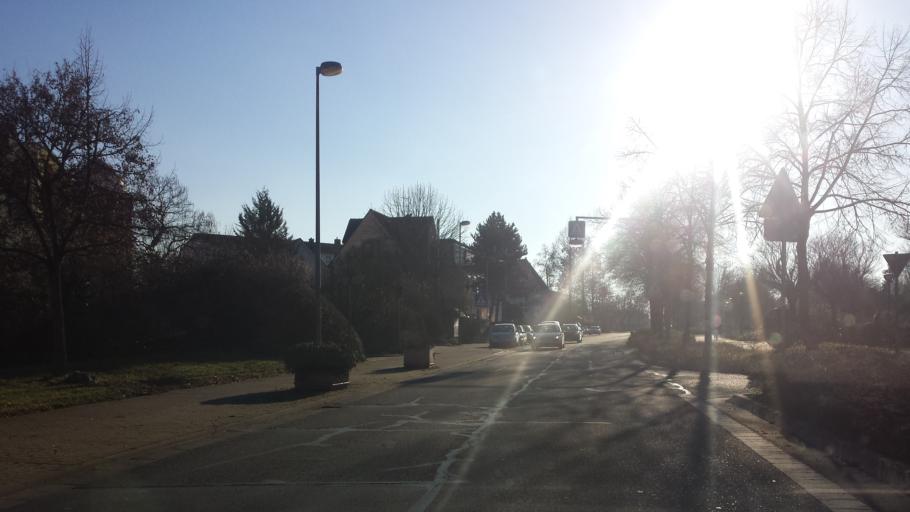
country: DE
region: Baden-Wuerttemberg
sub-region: Karlsruhe Region
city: Hockenheim
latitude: 49.3183
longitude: 8.5391
